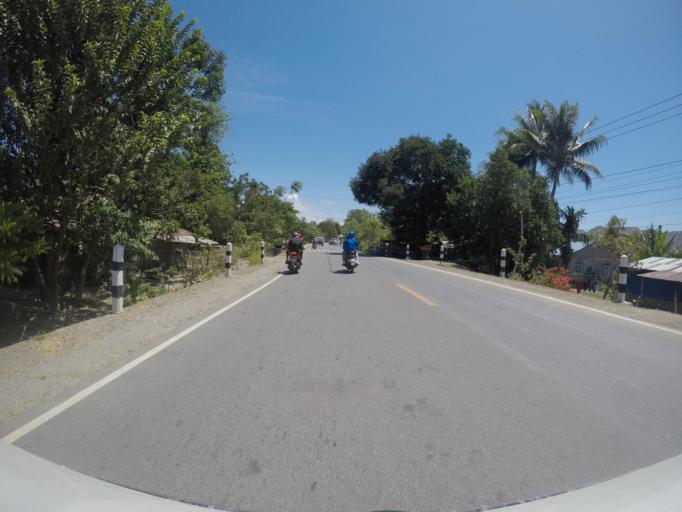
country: ID
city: Metinaro
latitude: -8.5422
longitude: 125.6769
